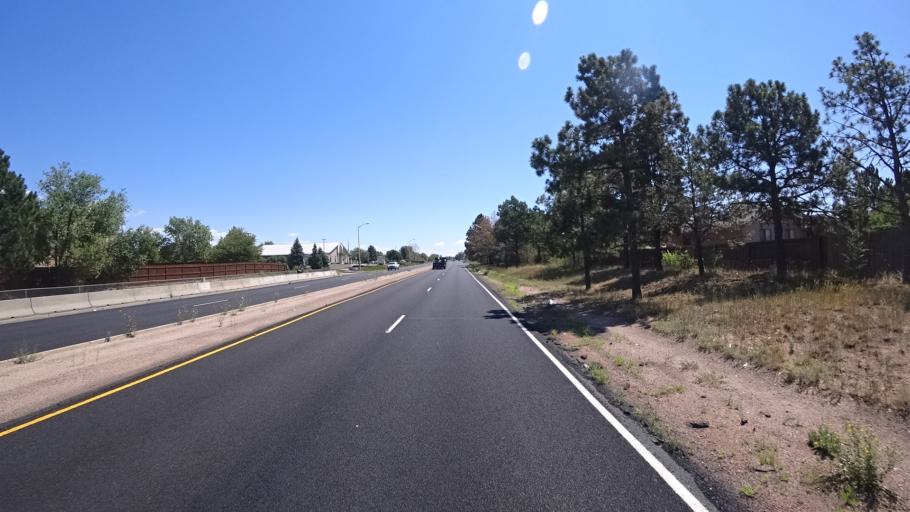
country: US
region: Colorado
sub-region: El Paso County
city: Stratmoor
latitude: 38.7889
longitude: -104.7501
